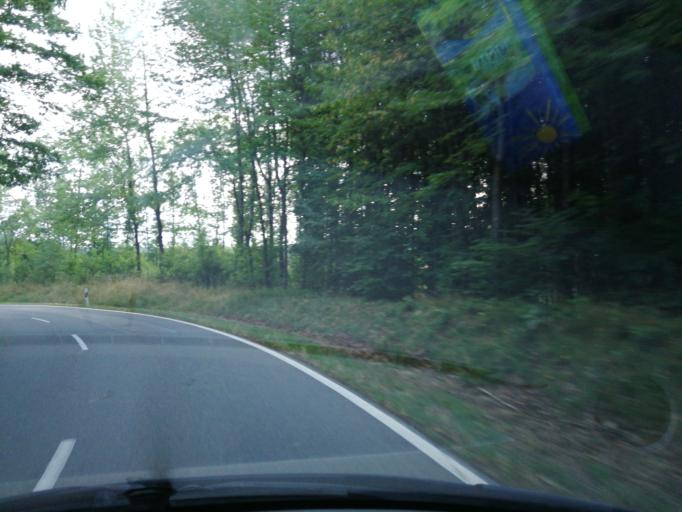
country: DE
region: Bavaria
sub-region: Lower Bavaria
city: Haibach
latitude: 49.0364
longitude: 12.7223
